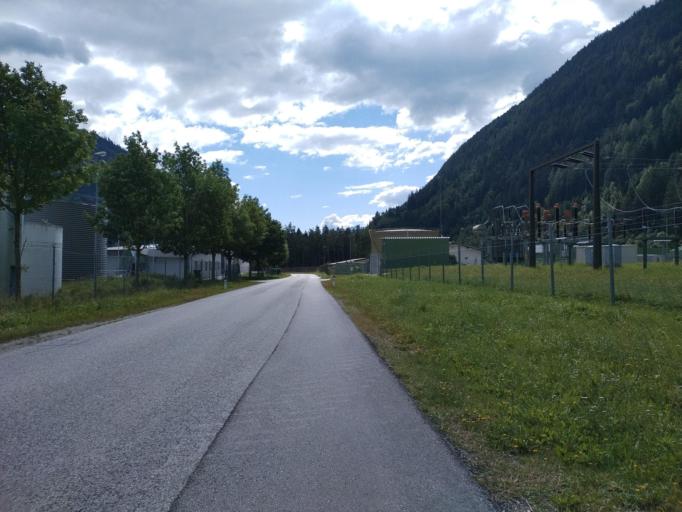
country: AT
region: Tyrol
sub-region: Politischer Bezirk Lienz
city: Hopfgarten in Defereggen
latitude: 46.9240
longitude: 12.5915
